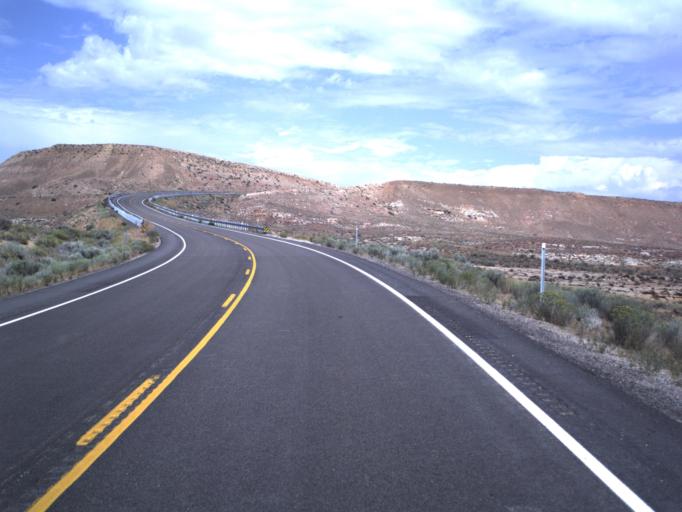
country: US
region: Utah
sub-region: Uintah County
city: Naples
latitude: 40.2668
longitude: -109.4544
